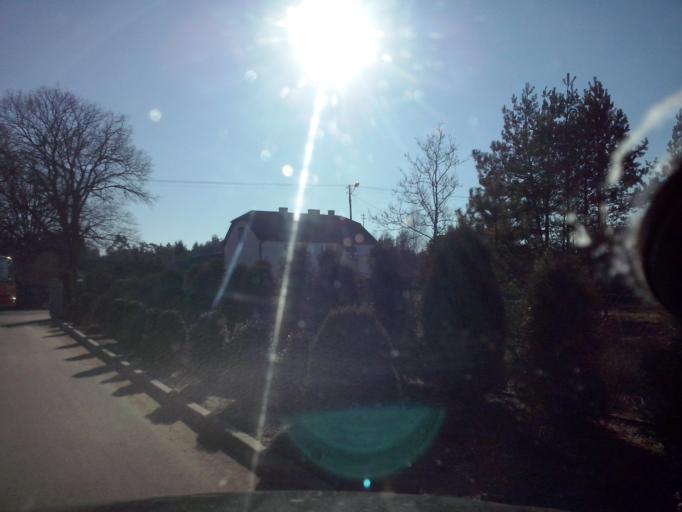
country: PL
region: Subcarpathian Voivodeship
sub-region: Powiat nizanski
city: Harasiuki
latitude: 50.4748
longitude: 22.4773
